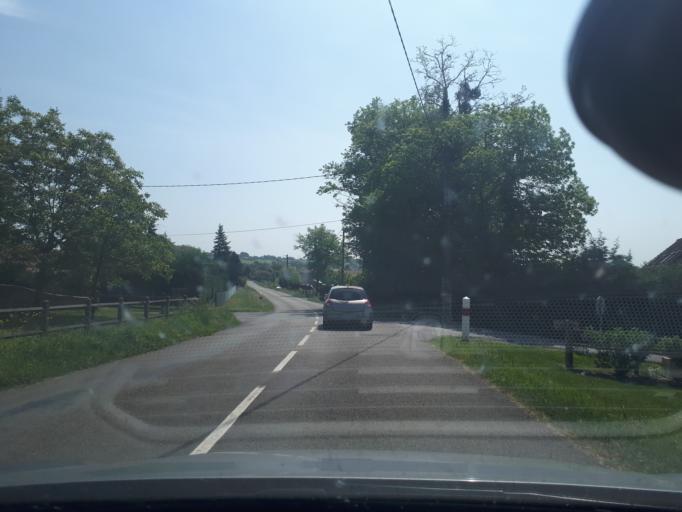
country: FR
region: Pays de la Loire
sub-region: Departement de la Sarthe
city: Le Breil-sur-Merize
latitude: 48.0198
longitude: 0.4567
